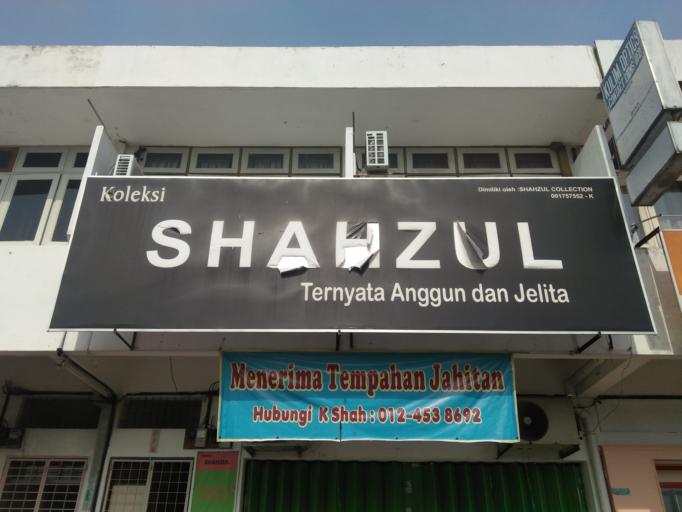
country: MY
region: Kedah
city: Kulim
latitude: 5.3715
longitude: 100.5561
